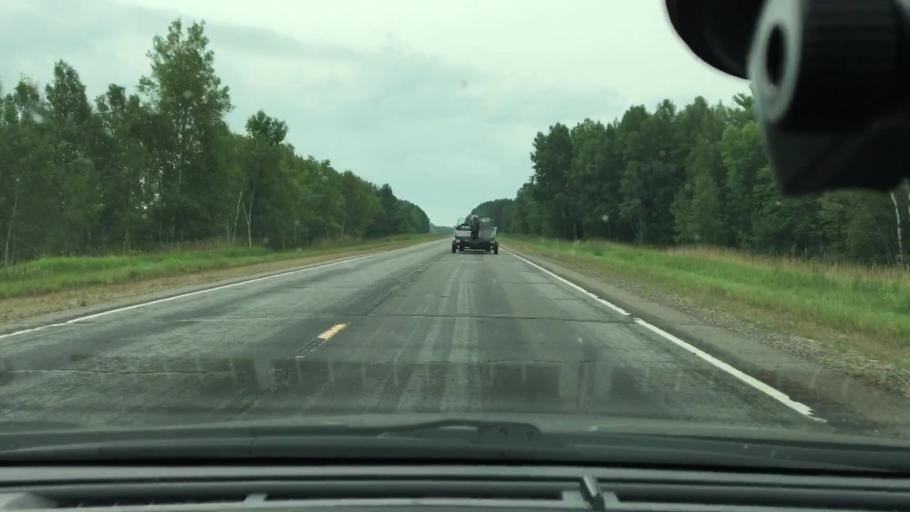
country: US
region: Minnesota
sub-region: Crow Wing County
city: Crosby
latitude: 46.6408
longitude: -93.9507
